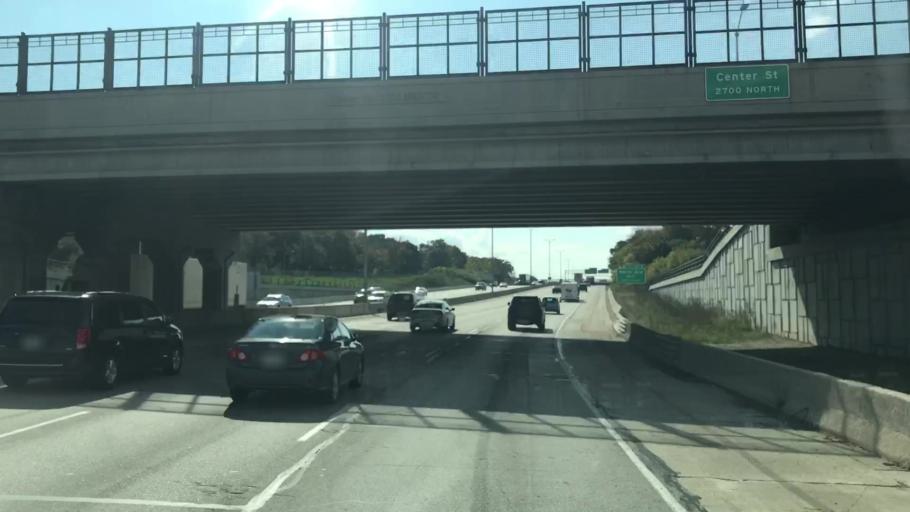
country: US
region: Wisconsin
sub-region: Waukesha County
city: Elm Grove
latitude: 43.0676
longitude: -88.0536
